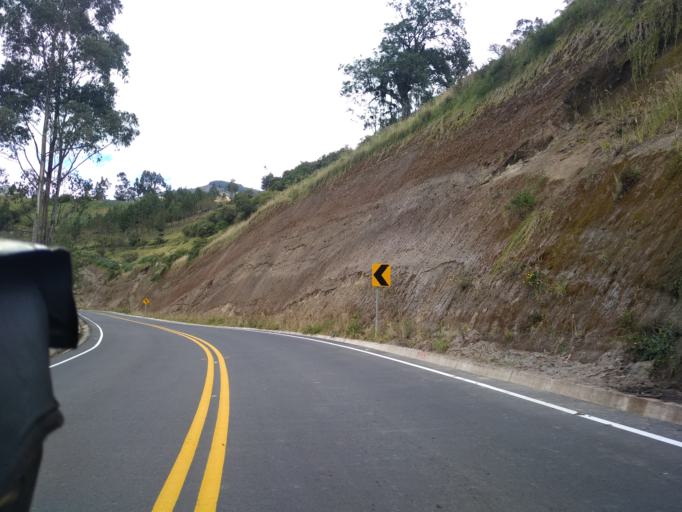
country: EC
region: Cotopaxi
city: Saquisili
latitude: -0.7240
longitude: -78.8947
